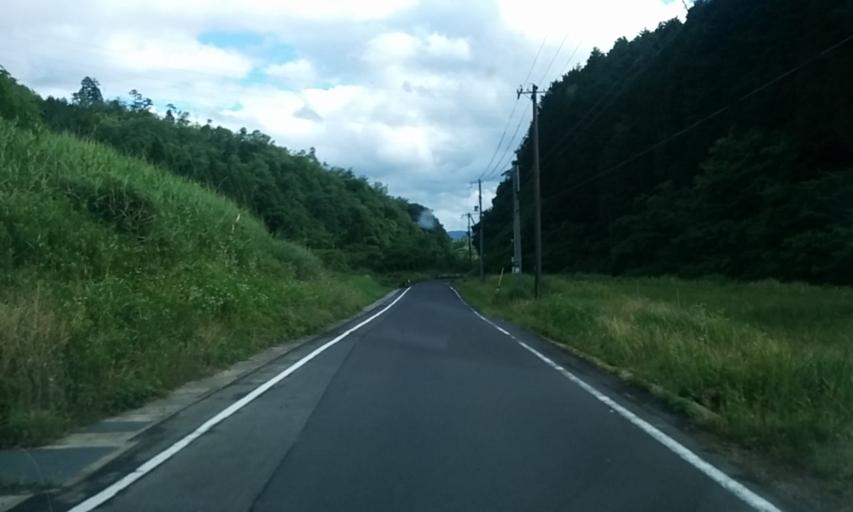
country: JP
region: Kyoto
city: Ayabe
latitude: 35.3679
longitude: 135.2886
